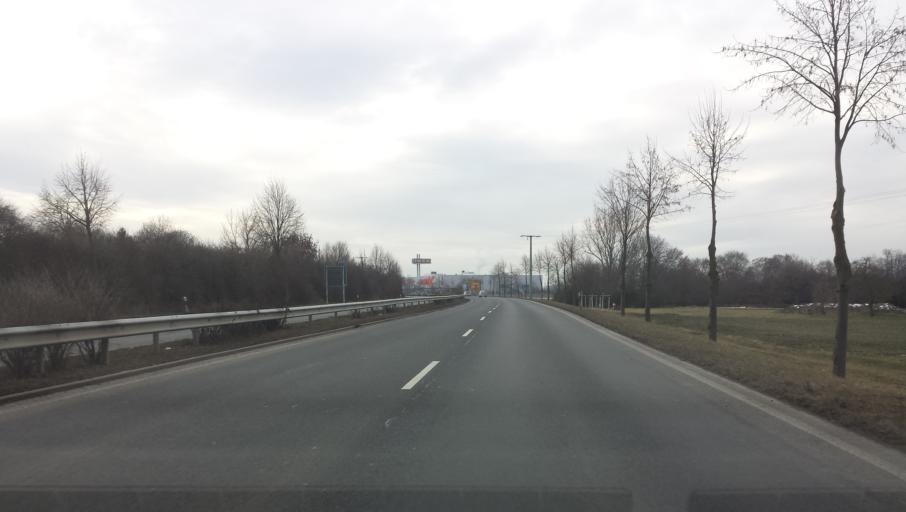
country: DE
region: Hesse
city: Lampertheim
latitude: 49.5639
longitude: 8.4462
